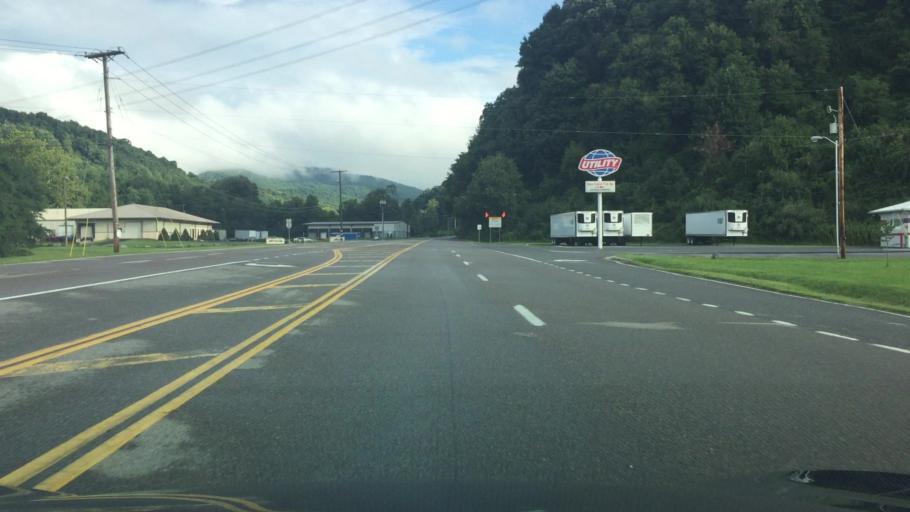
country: US
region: Virginia
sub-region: Smyth County
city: Atkins
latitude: 36.8612
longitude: -81.4332
